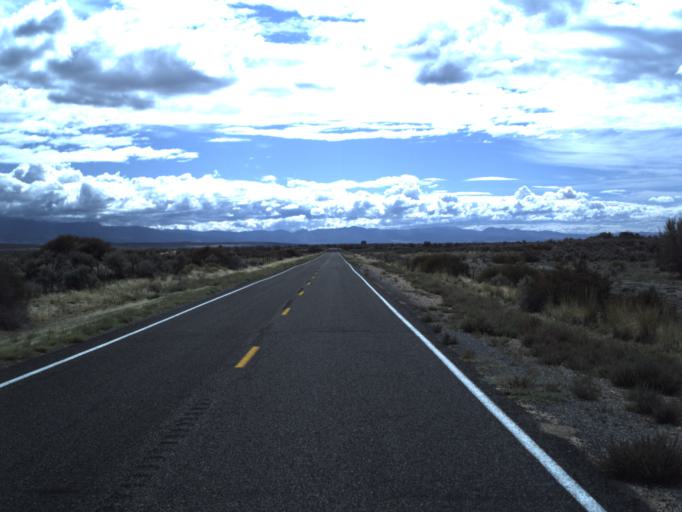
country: US
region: Utah
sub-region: Millard County
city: Fillmore
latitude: 39.1138
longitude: -112.4095
